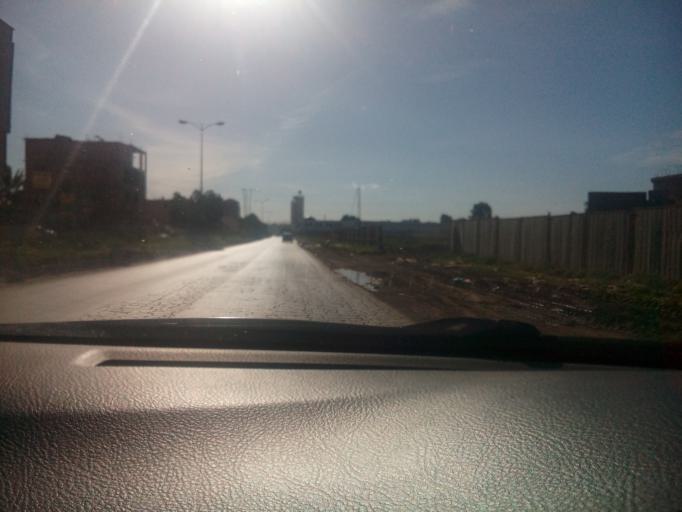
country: DZ
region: Oran
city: Sidi ech Chahmi
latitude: 35.6565
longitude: -0.5678
